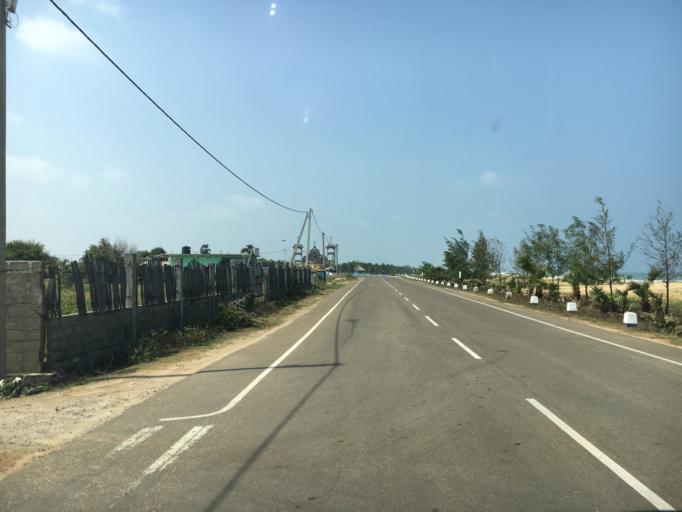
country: LK
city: Padaviya Divisional Secretariat
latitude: 9.2733
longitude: 80.8181
